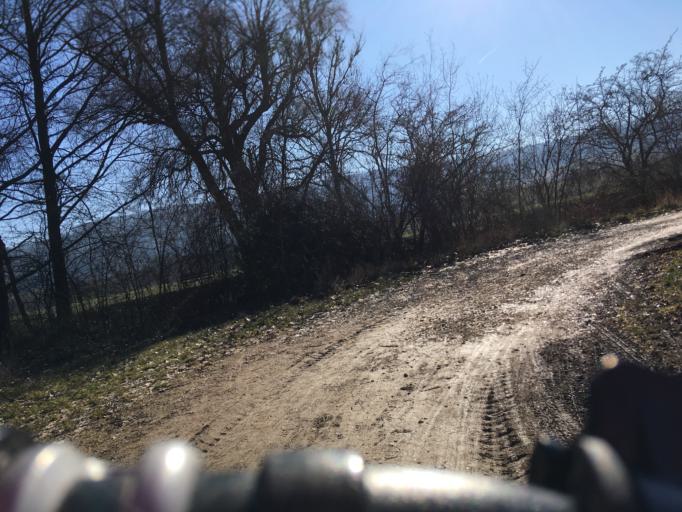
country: DE
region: Baden-Wuerttemberg
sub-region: Freiburg Region
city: Gottmadingen
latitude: 47.7222
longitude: 8.7708
